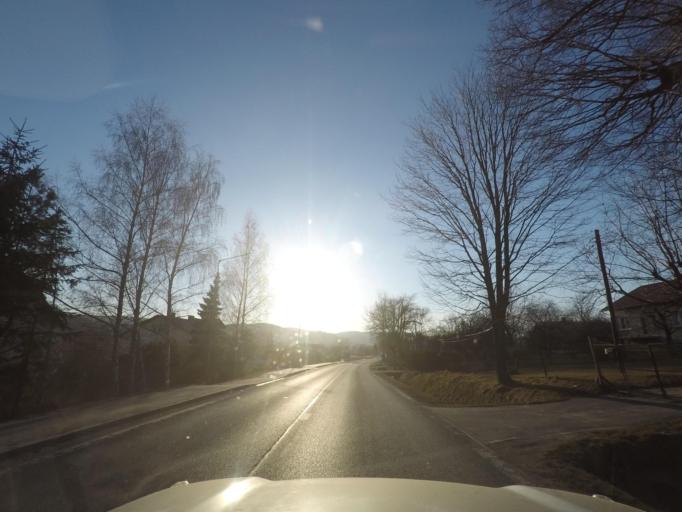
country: PL
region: Subcarpathian Voivodeship
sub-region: Powiat krosnienski
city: Dukla
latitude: 49.5576
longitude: 21.6469
